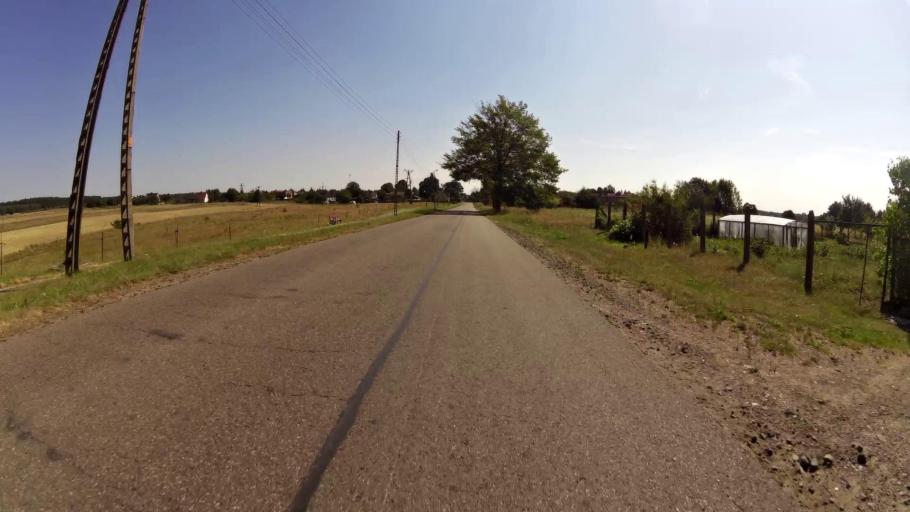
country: PL
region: West Pomeranian Voivodeship
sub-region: Powiat drawski
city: Czaplinek
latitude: 53.4435
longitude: 16.2624
